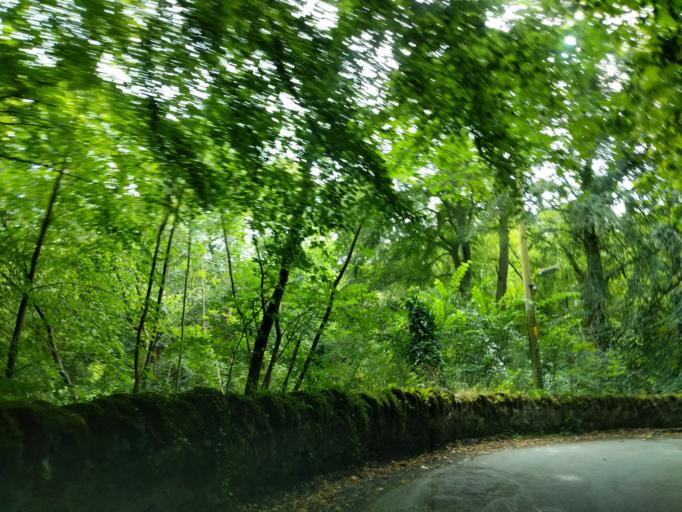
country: GB
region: Scotland
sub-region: Midlothian
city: Loanhead
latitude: 55.8718
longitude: -3.1428
